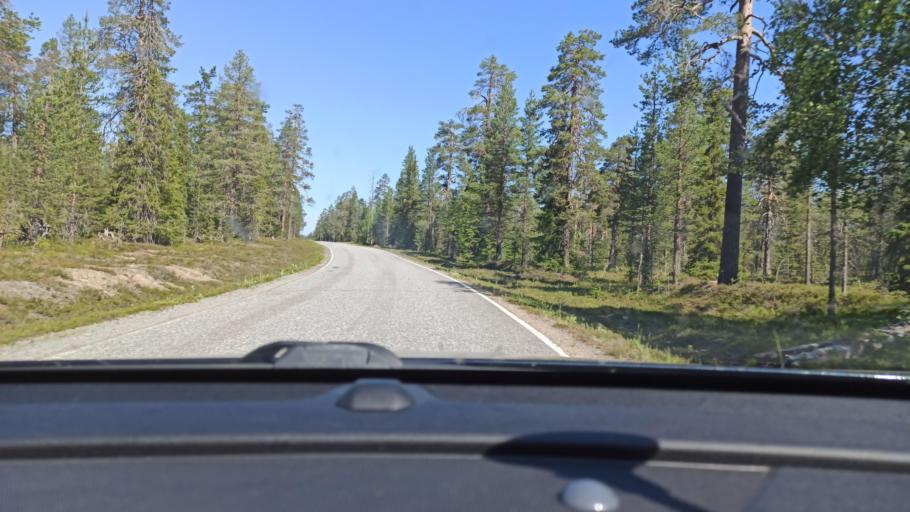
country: FI
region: Lapland
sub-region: Tunturi-Lappi
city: Kolari
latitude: 67.6598
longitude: 24.1658
